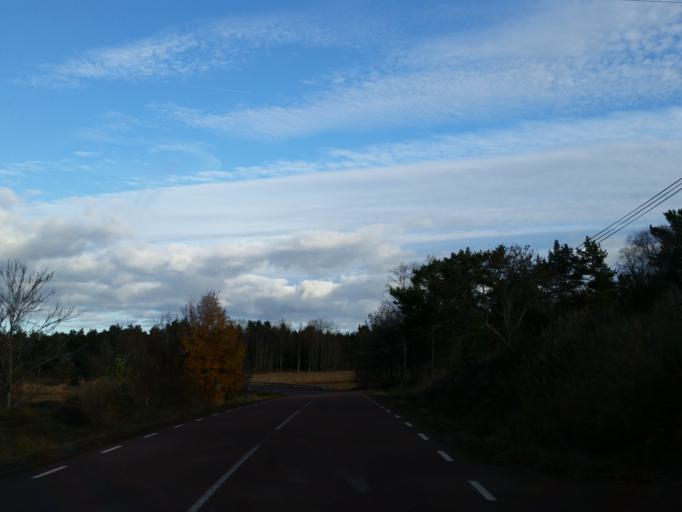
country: AX
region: Alands skaergard
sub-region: Foegloe
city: Foegloe
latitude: 60.0430
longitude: 20.5351
